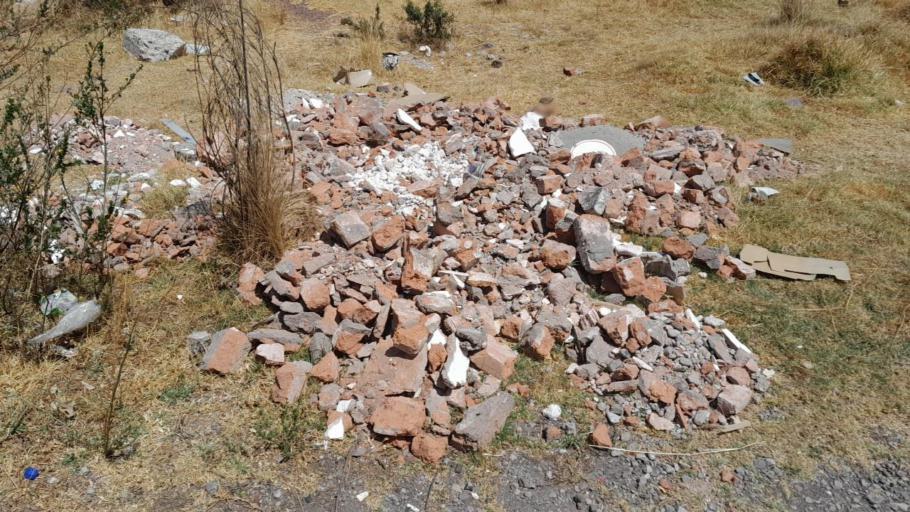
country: PE
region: Cusco
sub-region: Provincia de Cusco
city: Cusco
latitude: -13.4966
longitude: -71.9293
